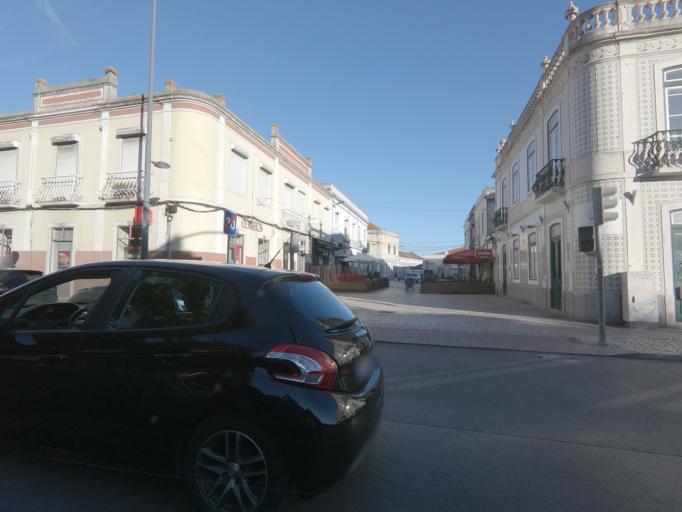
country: PT
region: Setubal
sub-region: Setubal
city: Setubal
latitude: 38.5211
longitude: -8.9009
